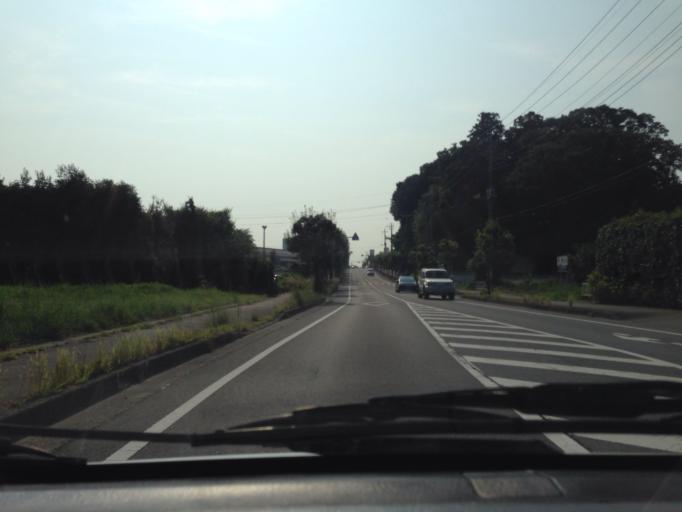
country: JP
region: Ibaraki
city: Ami
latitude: 36.0615
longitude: 140.1987
